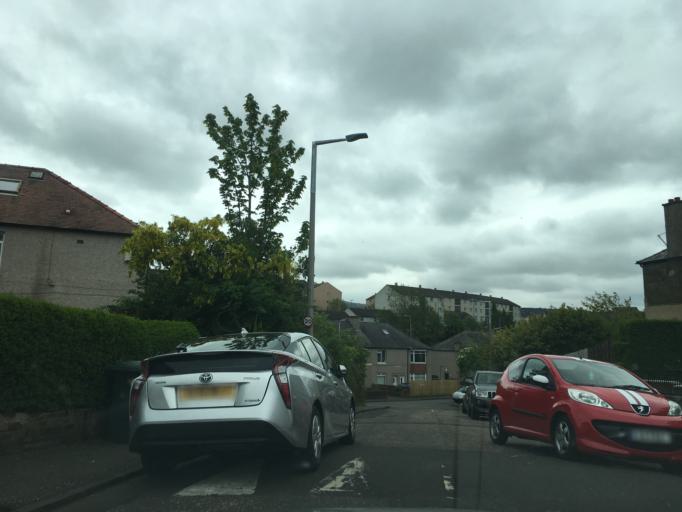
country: GB
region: Scotland
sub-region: Edinburgh
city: Colinton
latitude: 55.9202
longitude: -3.2836
